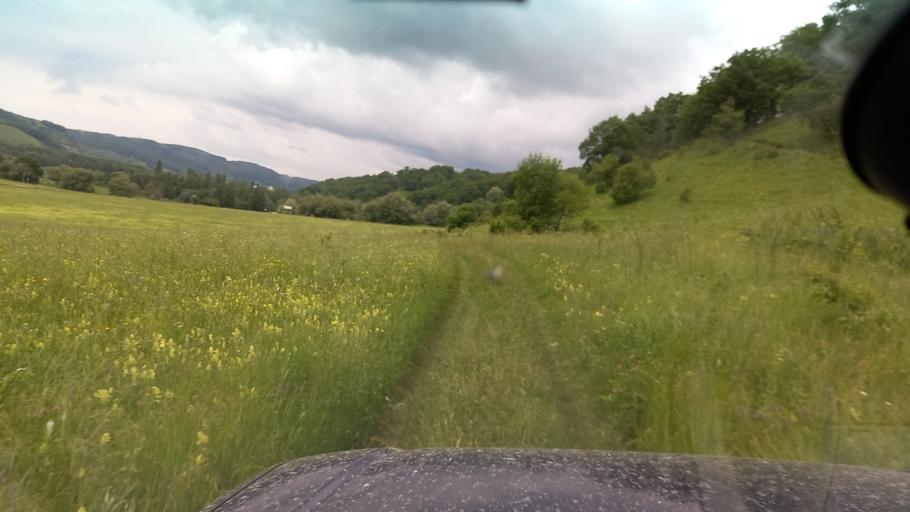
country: RU
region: Krasnodarskiy
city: Psebay
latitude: 44.1518
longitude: 40.8572
